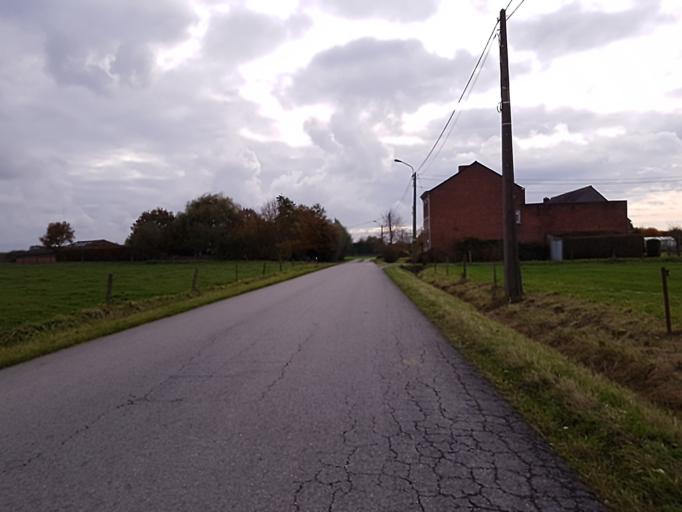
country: BE
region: Flanders
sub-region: Provincie Antwerpen
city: Lint
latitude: 51.1206
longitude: 4.5261
